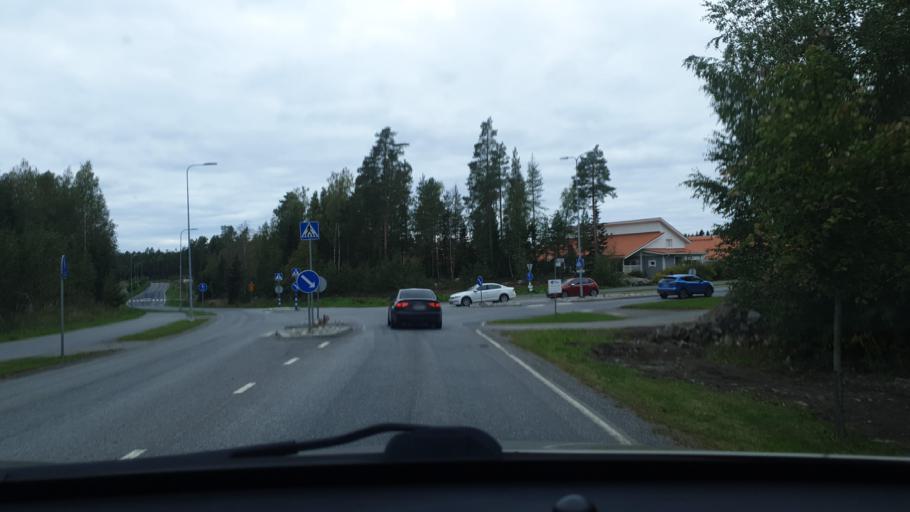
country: FI
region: Ostrobothnia
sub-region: Vaasa
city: Korsholm
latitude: 63.1193
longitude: 21.6576
